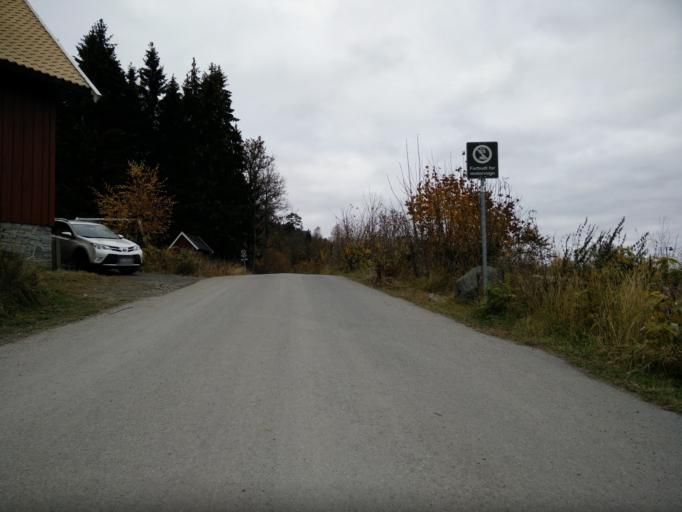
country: NO
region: Akershus
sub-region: Baerum
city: Sandvika
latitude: 59.9325
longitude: 10.5597
